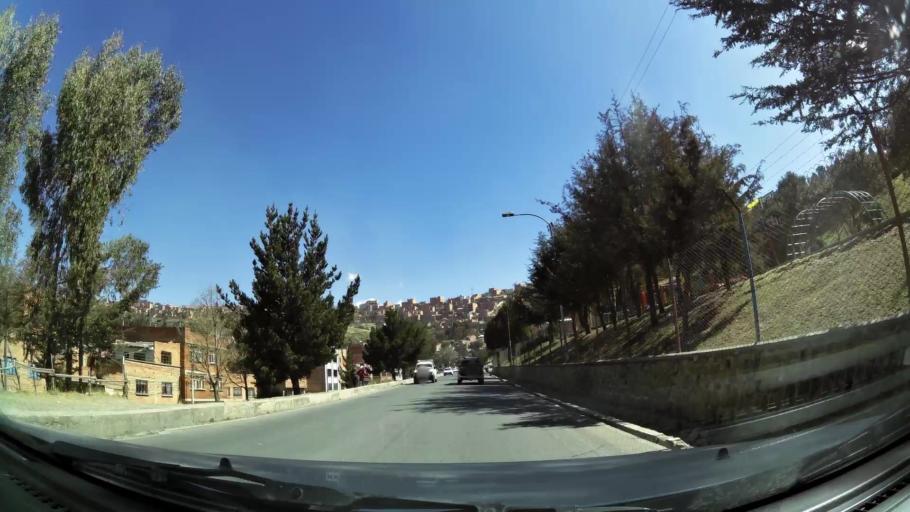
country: BO
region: La Paz
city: La Paz
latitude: -16.4872
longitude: -68.1657
